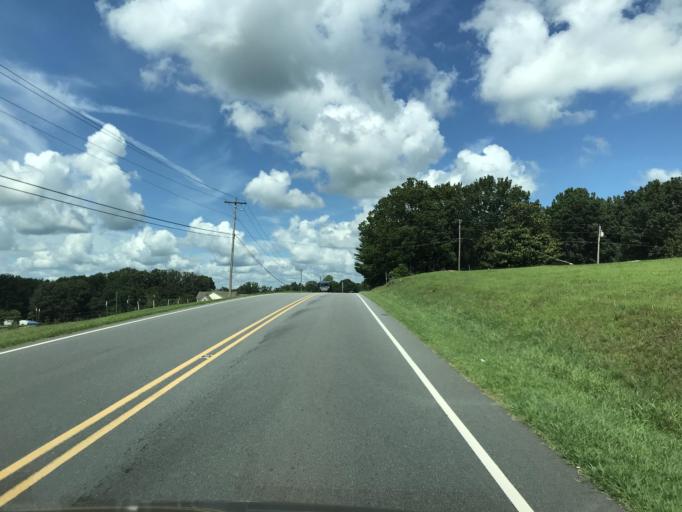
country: US
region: North Carolina
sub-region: Lincoln County
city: Pumpkin Center
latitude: 35.5334
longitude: -81.1298
